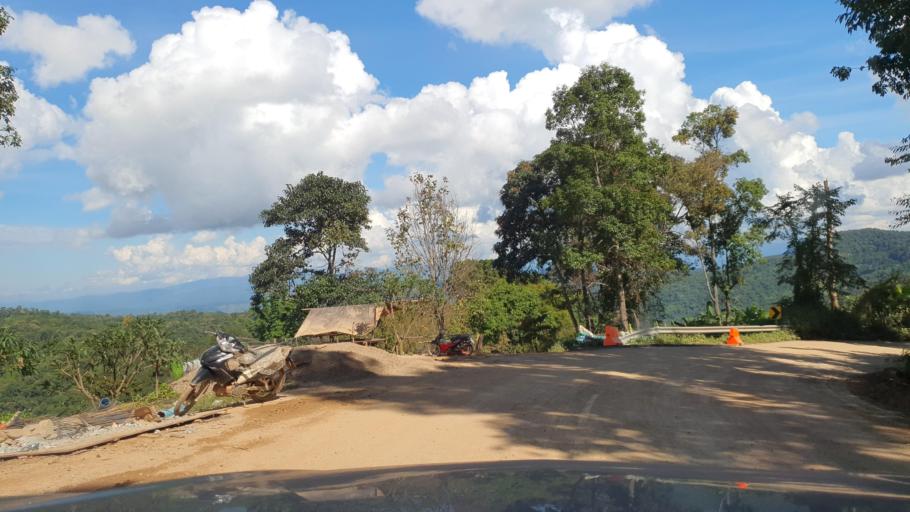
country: TH
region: Chiang Mai
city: Phrao
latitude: 19.3114
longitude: 99.3350
